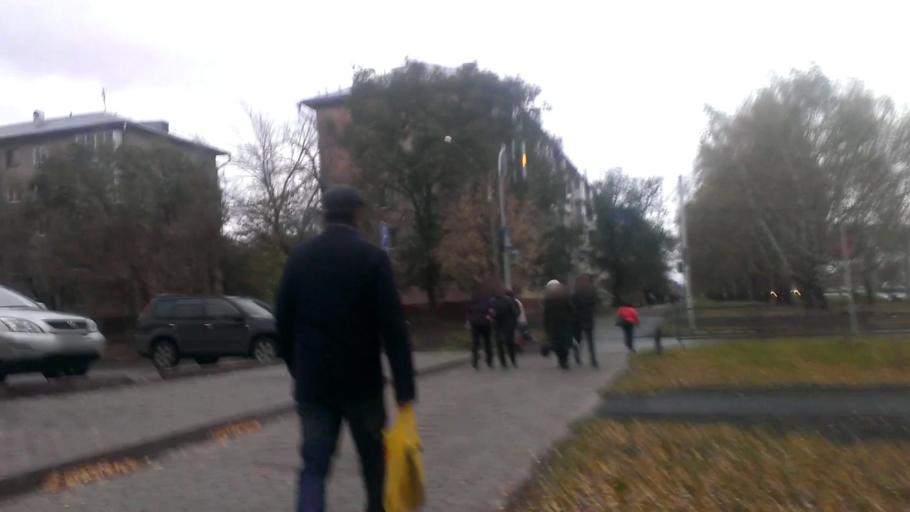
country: RU
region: Altai Krai
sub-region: Gorod Barnaulskiy
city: Barnaul
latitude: 53.3609
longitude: 83.6912
